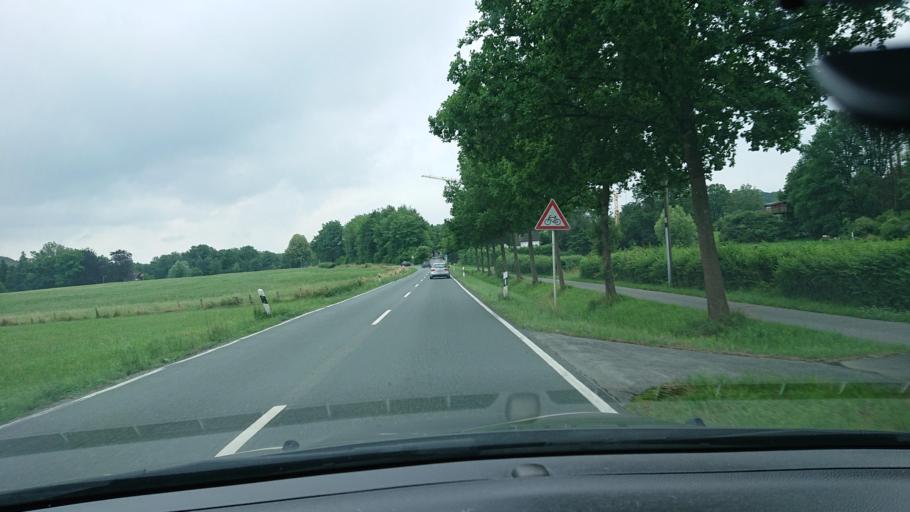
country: DE
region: North Rhine-Westphalia
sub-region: Regierungsbezirk Arnsberg
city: Mohnesee
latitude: 51.4734
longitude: 8.2286
